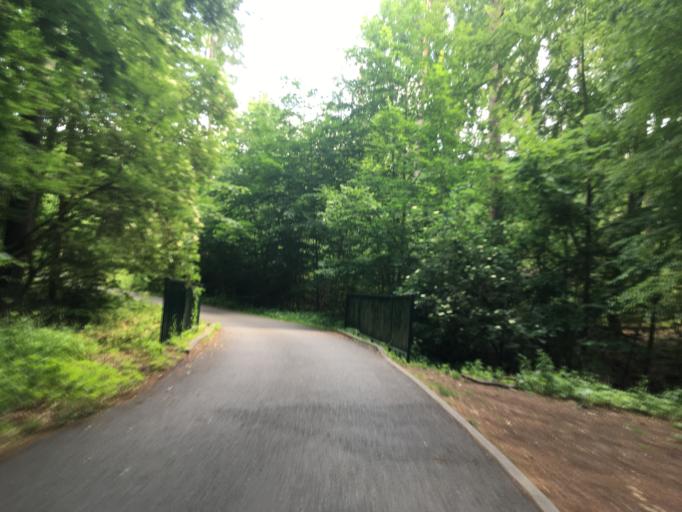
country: DE
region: Brandenburg
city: Waldsieversdorf
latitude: 52.5393
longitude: 14.0860
